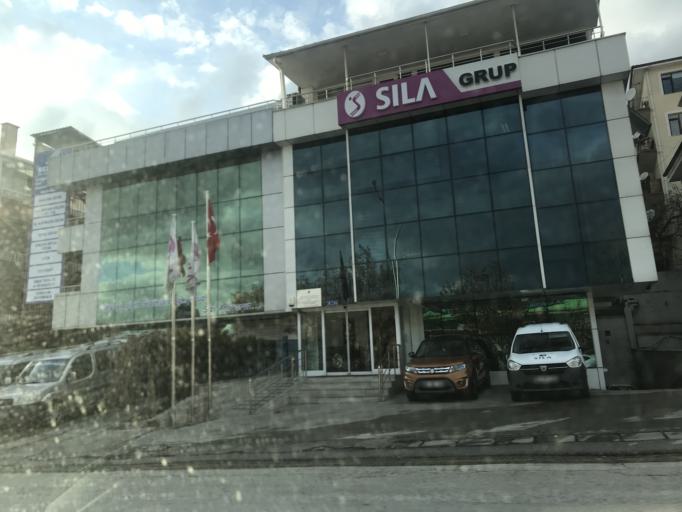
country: TR
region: Ankara
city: Mamak
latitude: 39.9684
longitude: 32.8751
